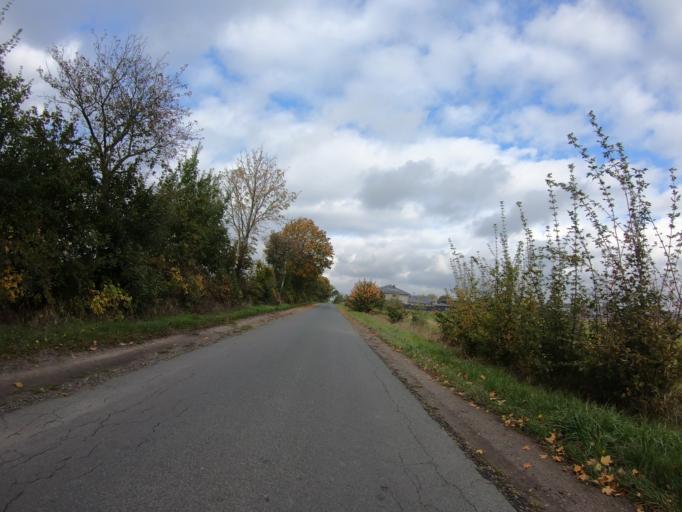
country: DE
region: Lower Saxony
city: Wahrenholz
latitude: 52.6165
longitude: 10.5924
